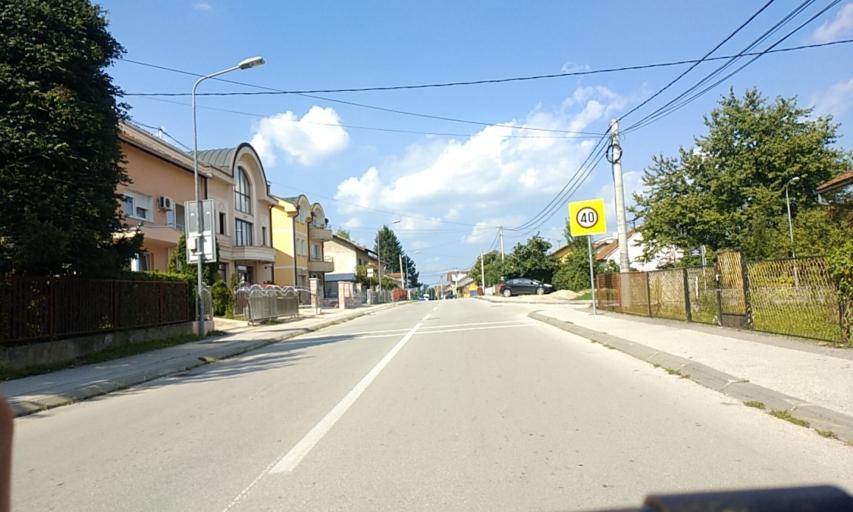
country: BA
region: Republika Srpska
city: Banja Luka
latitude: 44.7880
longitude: 17.1945
